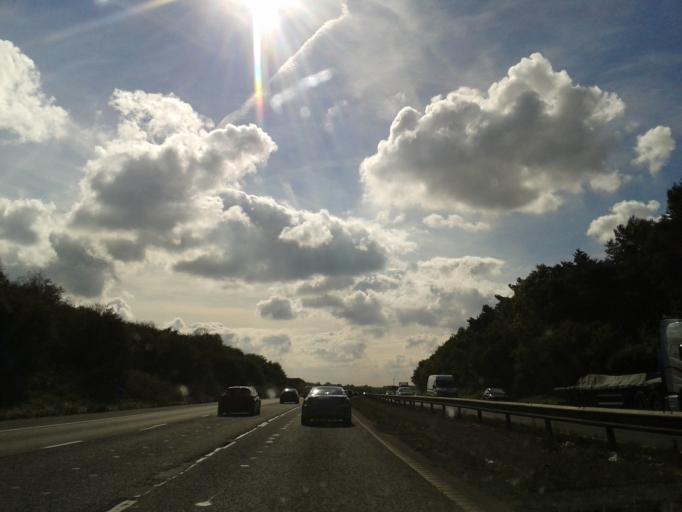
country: GB
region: England
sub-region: Staffordshire
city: Stone
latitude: 52.8788
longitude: -2.1652
